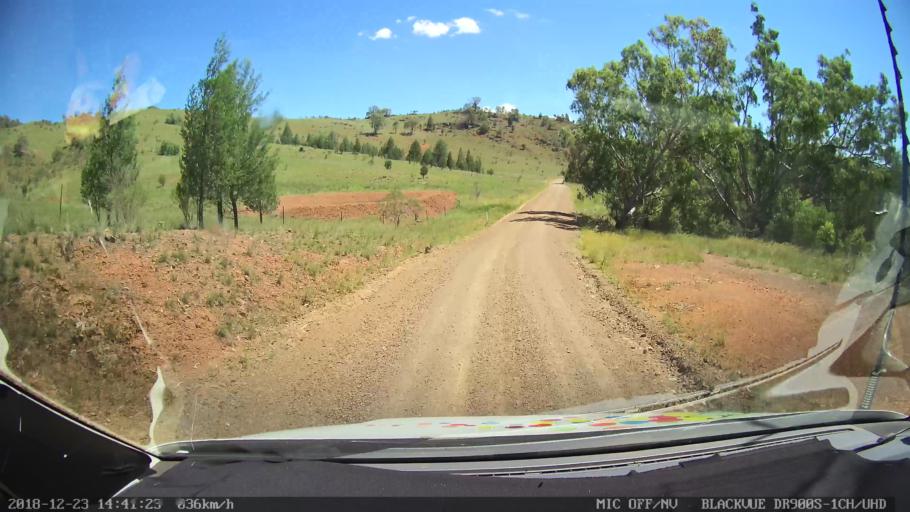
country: AU
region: New South Wales
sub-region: Tamworth Municipality
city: Manilla
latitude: -30.6311
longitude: 150.9022
